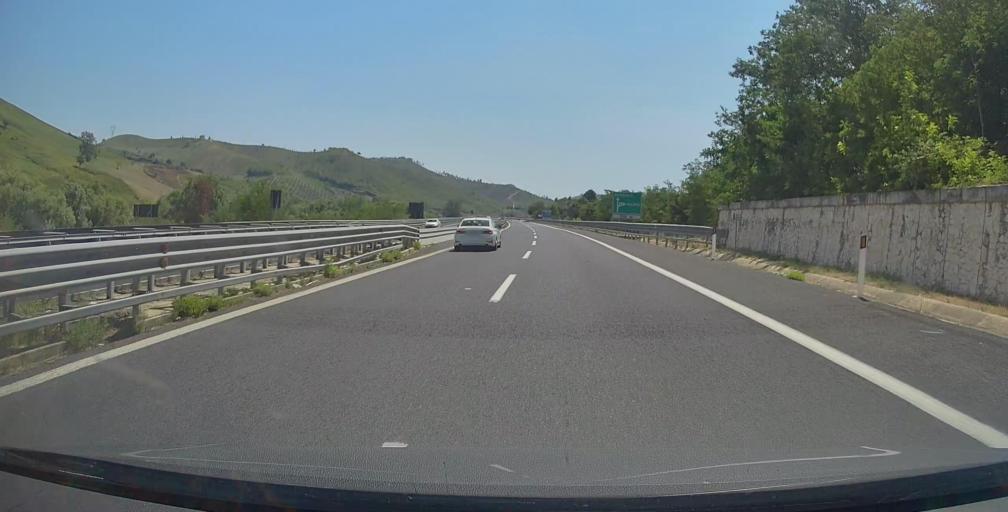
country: IT
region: Calabria
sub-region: Provincia di Vibo-Valentia
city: Paravati
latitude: 38.5705
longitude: 16.0896
